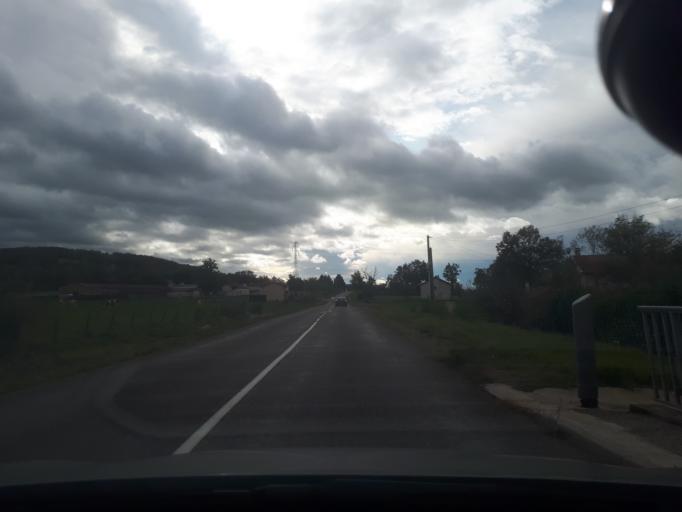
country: FR
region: Rhone-Alpes
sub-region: Departement de la Loire
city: Bellegarde-en-Forez
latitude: 45.7037
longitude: 4.3009
